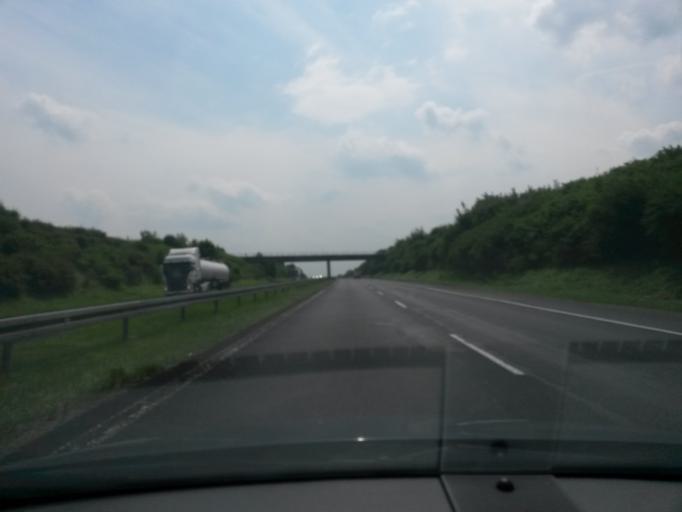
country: PL
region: Lodz Voivodeship
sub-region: Powiat radomszczanski
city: Kamiensk
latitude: 51.1957
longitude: 19.4746
